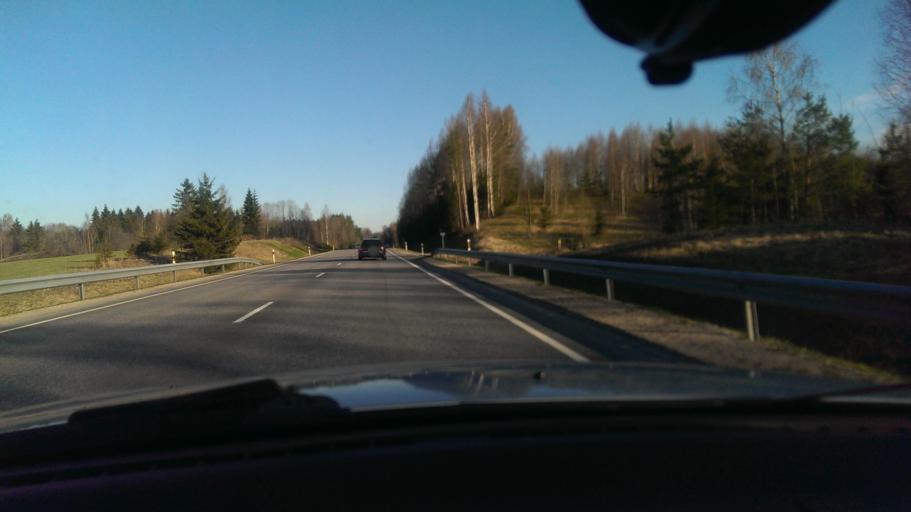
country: EE
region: Tartu
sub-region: UElenurme vald
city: Ulenurme
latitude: 58.1369
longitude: 26.7146
